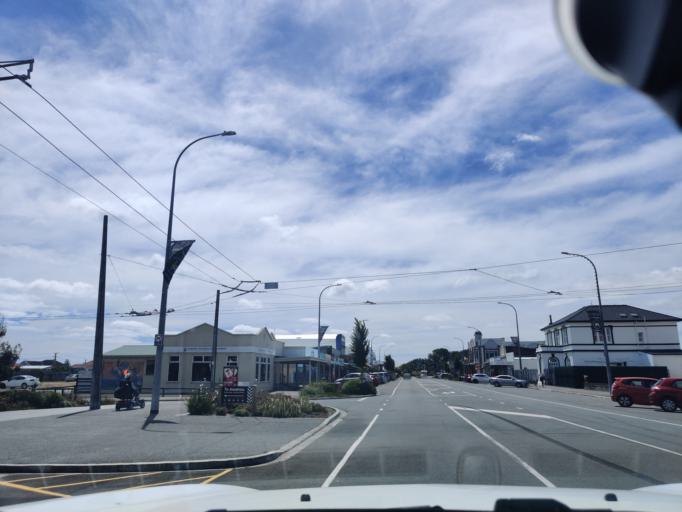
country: NZ
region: Manawatu-Wanganui
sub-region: Horowhenua District
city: Foxton
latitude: -40.4738
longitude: 175.2817
